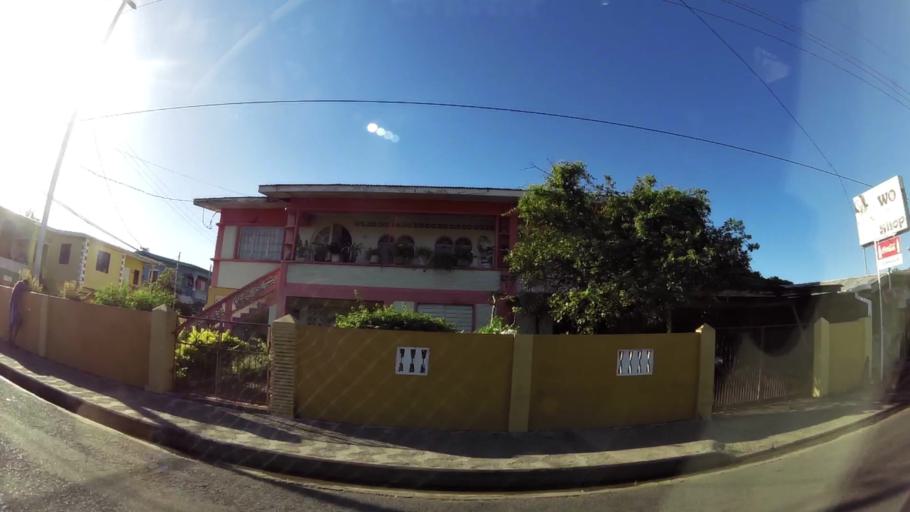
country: TT
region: Tobago
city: Scarborough
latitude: 11.1574
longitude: -60.8191
